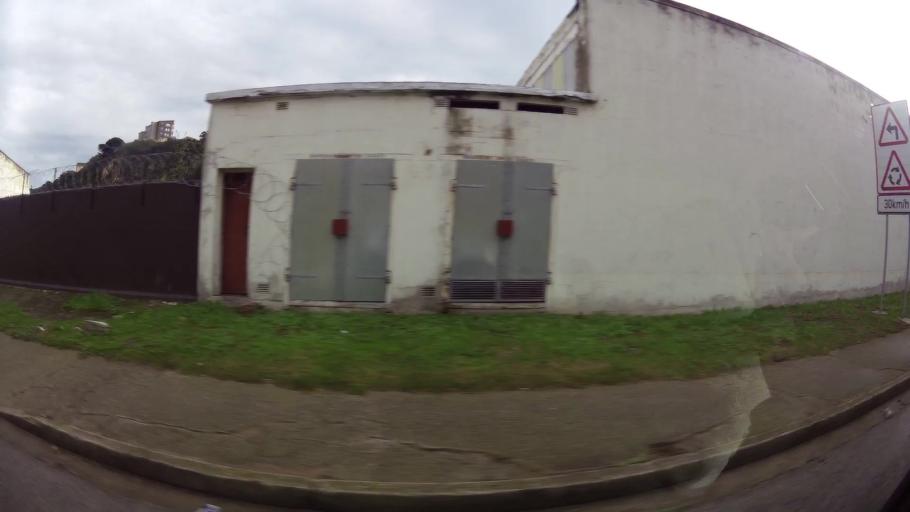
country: ZA
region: Eastern Cape
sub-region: Nelson Mandela Bay Metropolitan Municipality
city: Port Elizabeth
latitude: -33.9685
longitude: 25.6219
